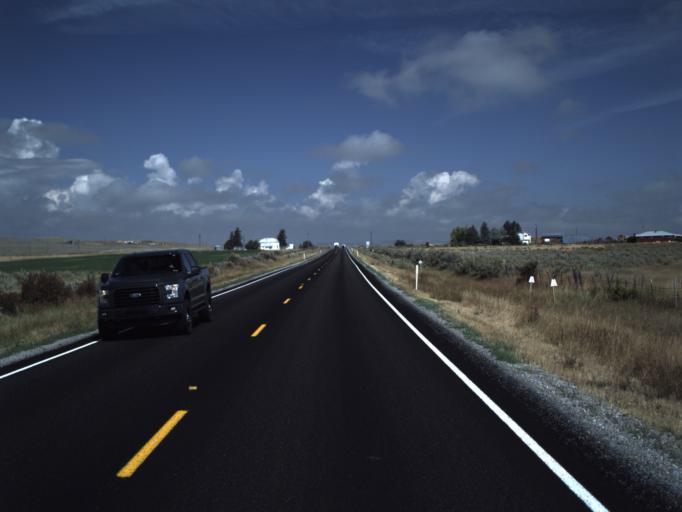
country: US
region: Utah
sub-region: Rich County
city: Randolph
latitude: 41.5949
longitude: -111.1734
